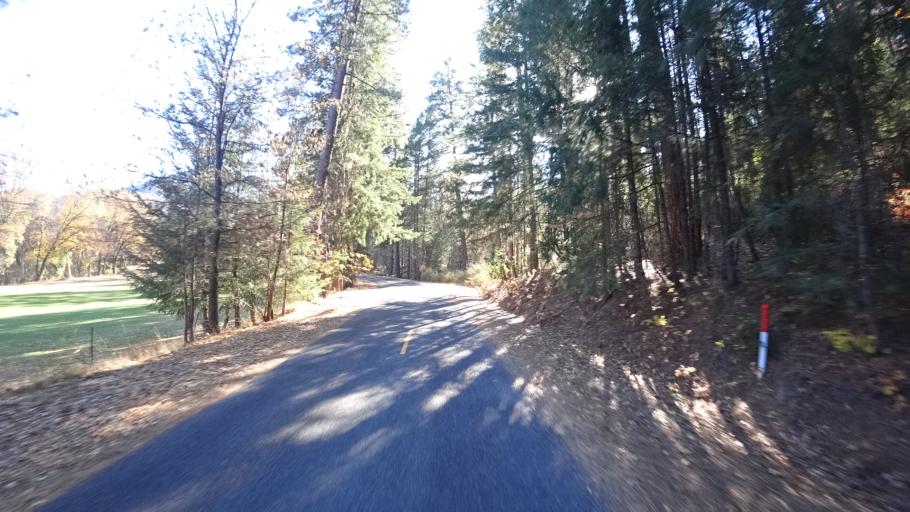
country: US
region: California
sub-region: Siskiyou County
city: Yreka
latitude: 41.8222
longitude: -122.9748
